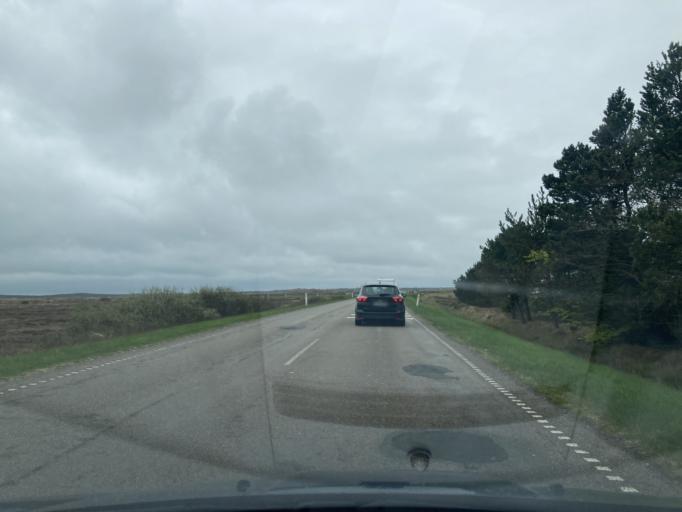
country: DK
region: North Denmark
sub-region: Thisted Kommune
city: Hanstholm
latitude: 57.0034
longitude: 8.4659
